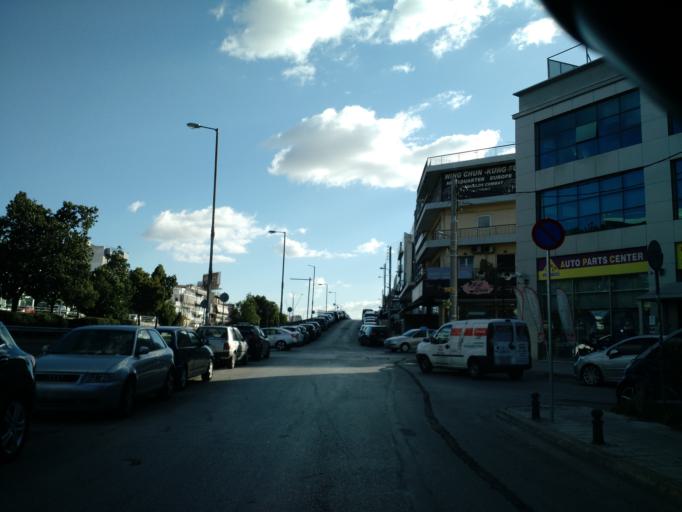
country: GR
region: Attica
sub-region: Nomarchia Athinas
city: Agios Dimitrios
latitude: 37.9332
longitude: 23.7442
